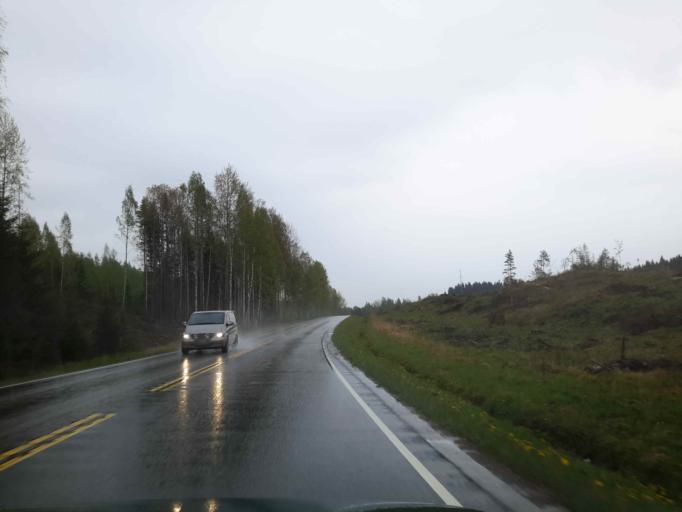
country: FI
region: Uusimaa
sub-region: Helsinki
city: Vihti
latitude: 60.3913
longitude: 24.4960
